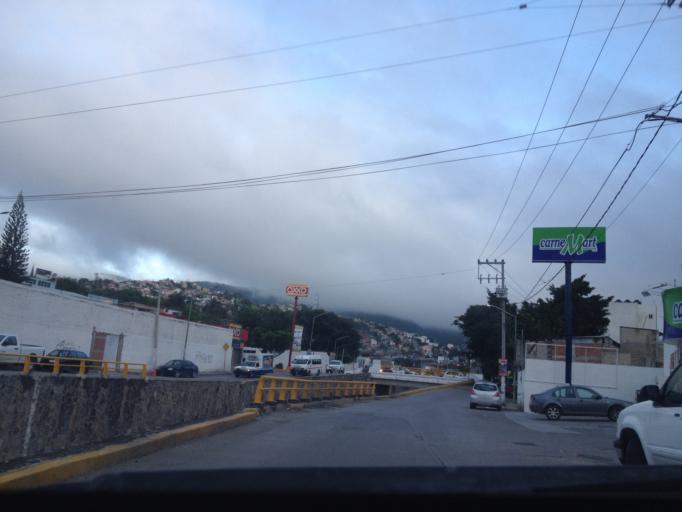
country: MX
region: Guerrero
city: Chilpancingo de los Bravos
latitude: 17.5492
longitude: -99.5034
